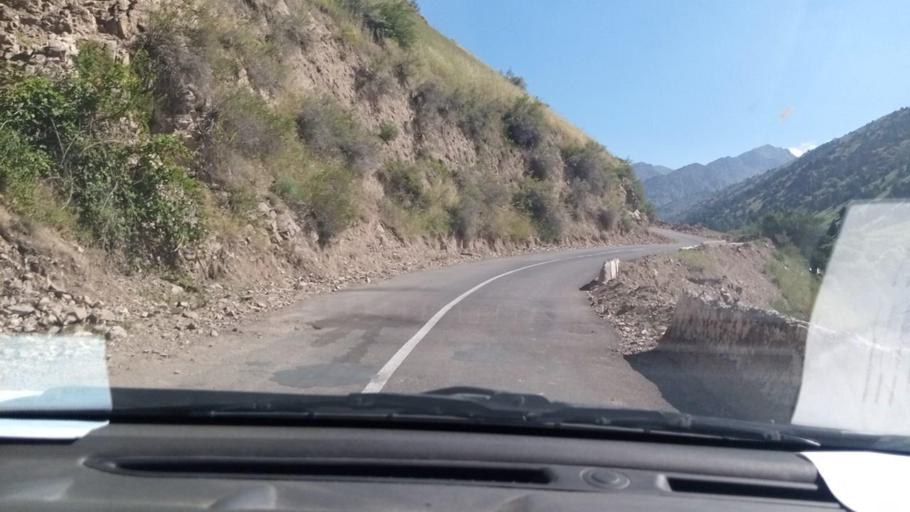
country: UZ
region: Toshkent
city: Yangiobod
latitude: 41.1252
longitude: 70.1066
